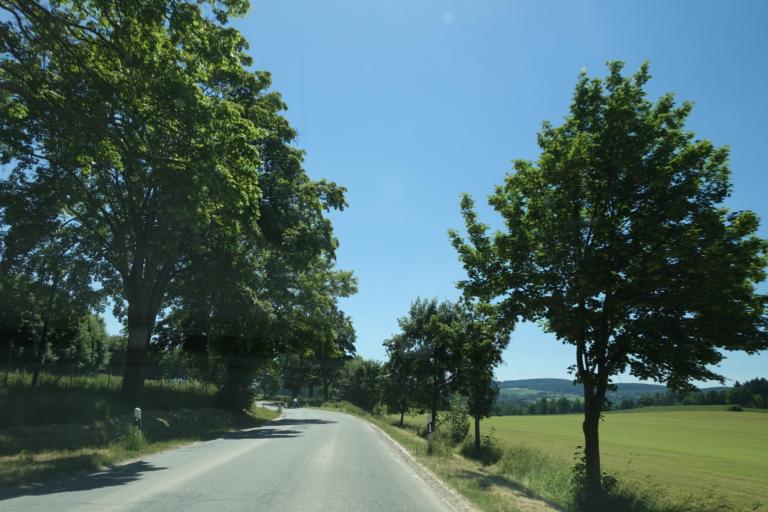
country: DE
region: Saxony
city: Borstendorf
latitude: 50.7897
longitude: 13.1708
